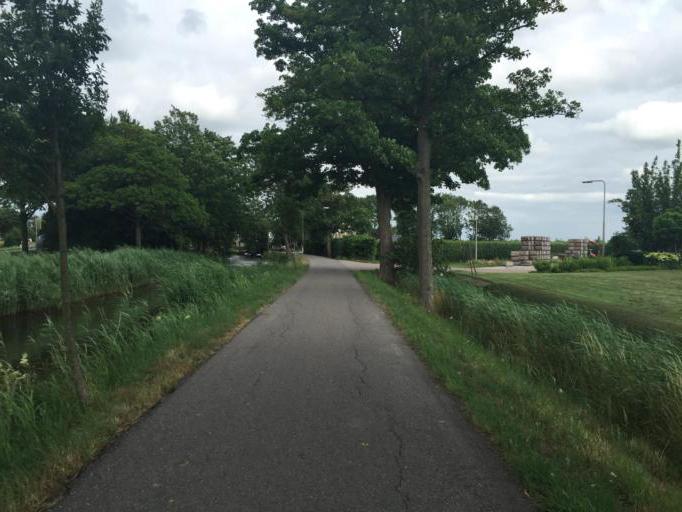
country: NL
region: Utrecht
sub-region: Gemeente Woerden
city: Woerden
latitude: 52.0590
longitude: 4.9120
